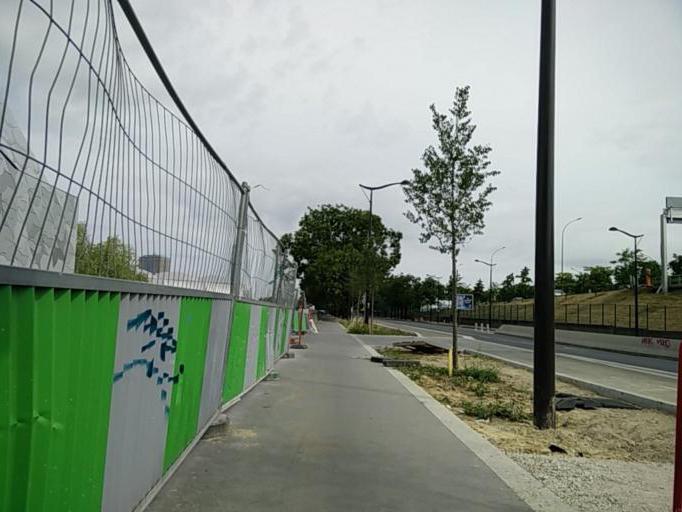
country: FR
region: Ile-de-France
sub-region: Departement de Seine-Saint-Denis
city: Le Pre-Saint-Gervais
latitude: 48.8925
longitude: 2.3947
